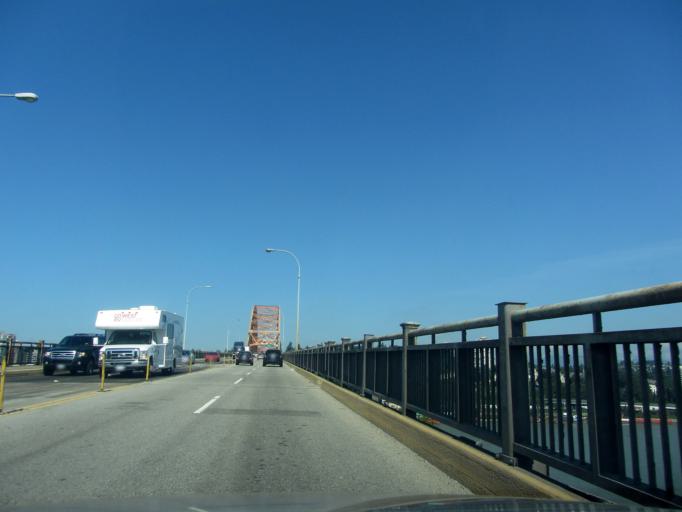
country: CA
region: British Columbia
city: New Westminster
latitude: 49.2064
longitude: -122.8913
